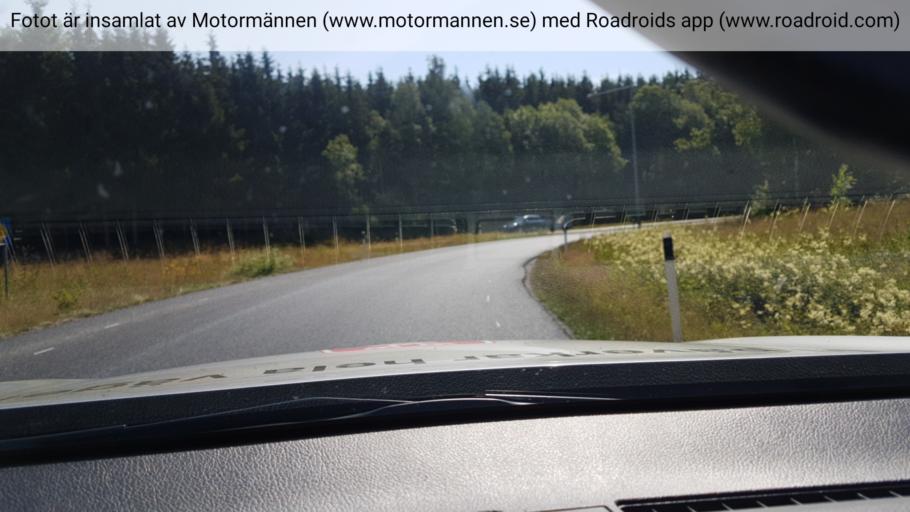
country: SE
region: Vaestra Goetaland
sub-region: Stenungsunds Kommun
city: Stora Hoga
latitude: 58.0575
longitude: 11.8811
